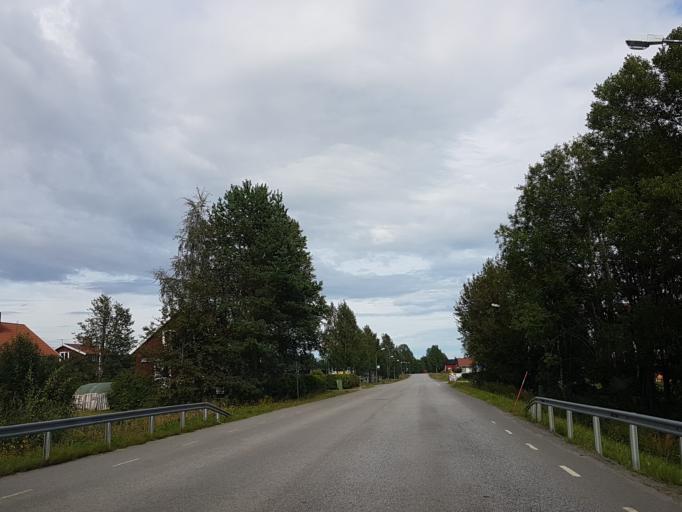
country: SE
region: Vaesterbotten
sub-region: Umea Kommun
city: Taftea
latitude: 63.8370
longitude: 20.4814
